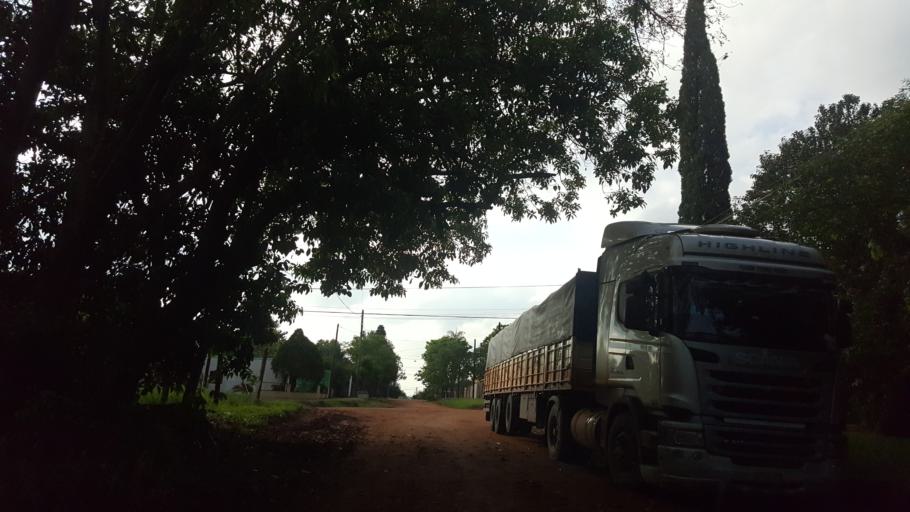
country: AR
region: Misiones
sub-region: Departamento de Capital
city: Posadas
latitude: -27.4262
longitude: -55.8991
